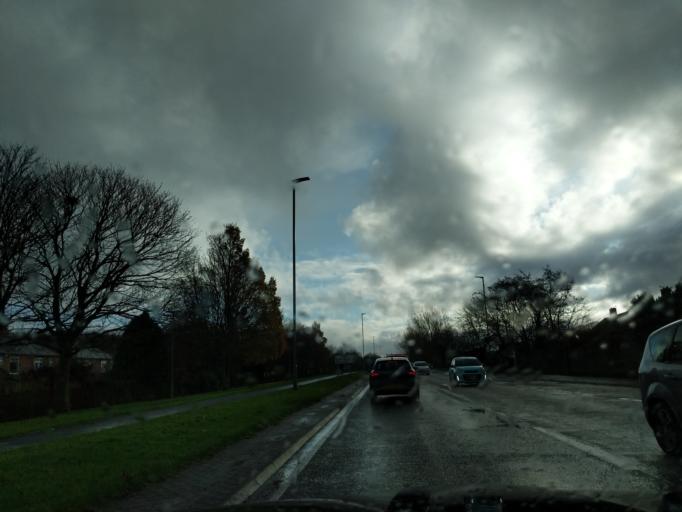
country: GB
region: England
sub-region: Northumberland
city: Blyth
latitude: 55.1186
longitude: -1.5113
